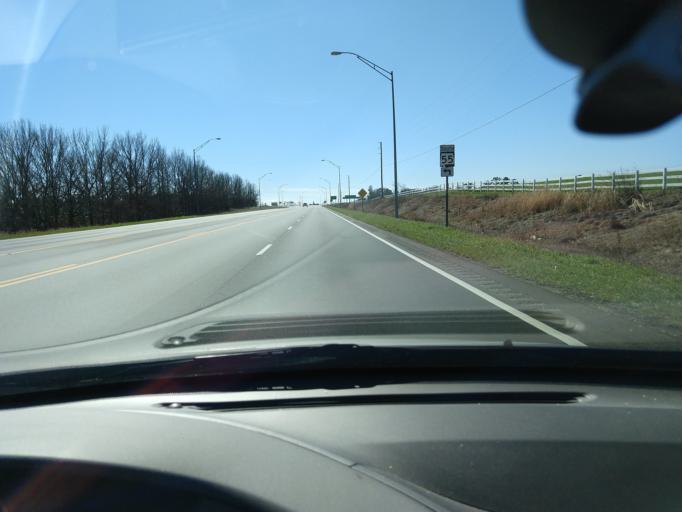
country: US
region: Alabama
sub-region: Covington County
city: Andalusia
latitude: 31.2810
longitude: -86.5055
